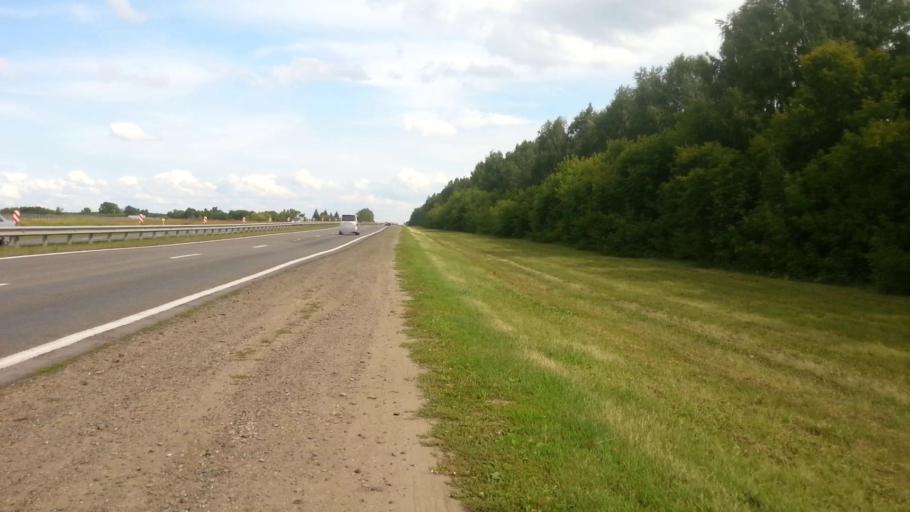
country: RU
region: Altai Krai
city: Nauchnyy Gorodok
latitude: 53.3559
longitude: 83.5183
